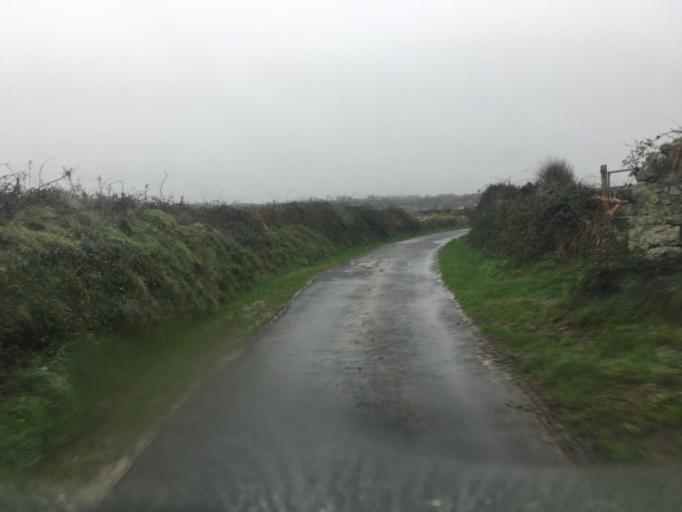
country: FR
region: Lower Normandy
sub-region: Departement de la Manche
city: Beaumont-Hague
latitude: 49.7198
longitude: -1.9204
